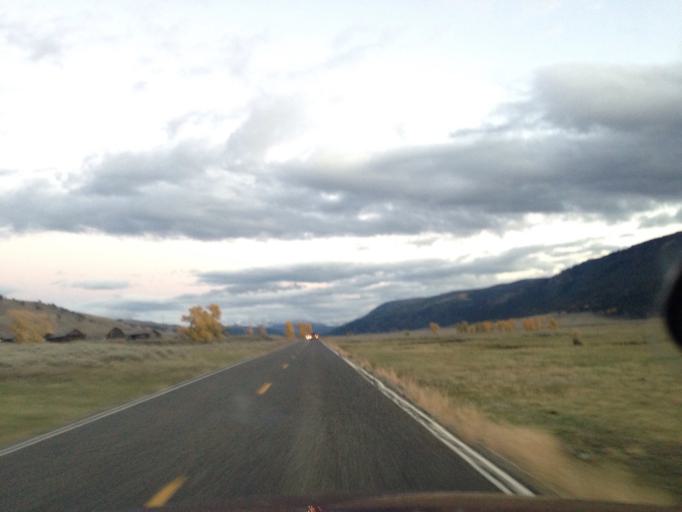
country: US
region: Montana
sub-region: Park County
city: Livingston
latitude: 44.8972
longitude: -110.2383
